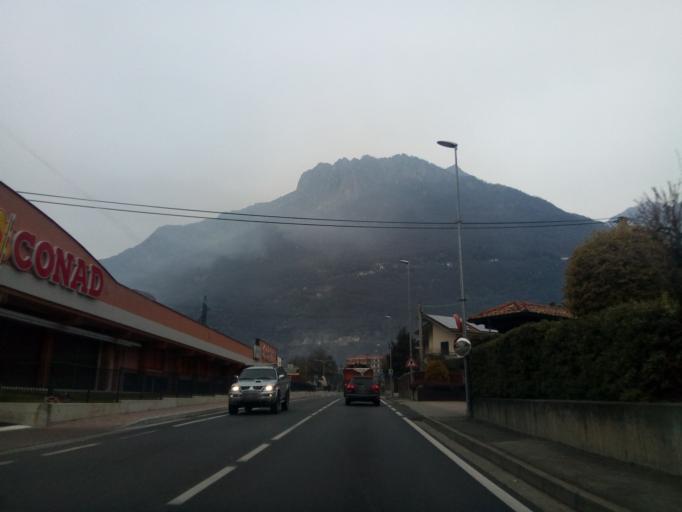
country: IT
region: Aosta Valley
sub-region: Valle d'Aosta
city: Pont-Saint-Martin
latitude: 45.5929
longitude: 7.7993
